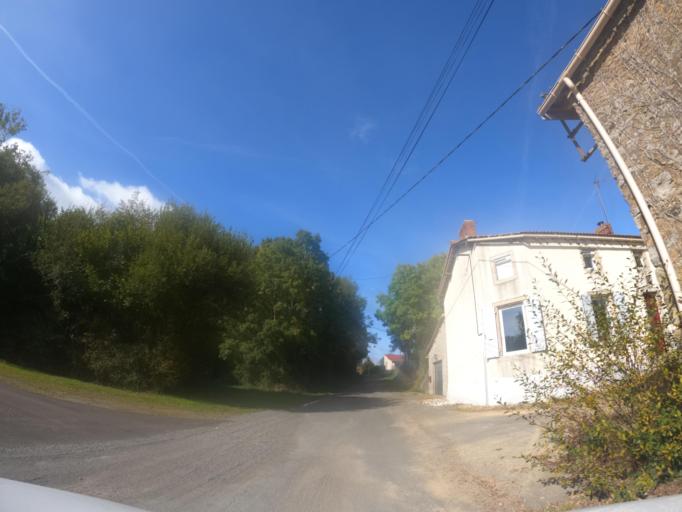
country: FR
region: Poitou-Charentes
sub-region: Departement des Deux-Sevres
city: Courlay
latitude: 46.7924
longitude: -0.5856
